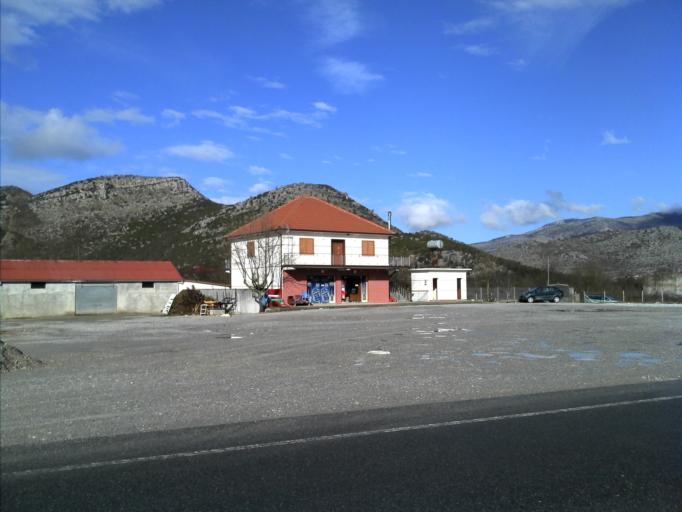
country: AL
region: Shkoder
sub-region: Rrethi i Malesia e Madhe
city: Hot
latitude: 42.3077
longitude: 19.4408
